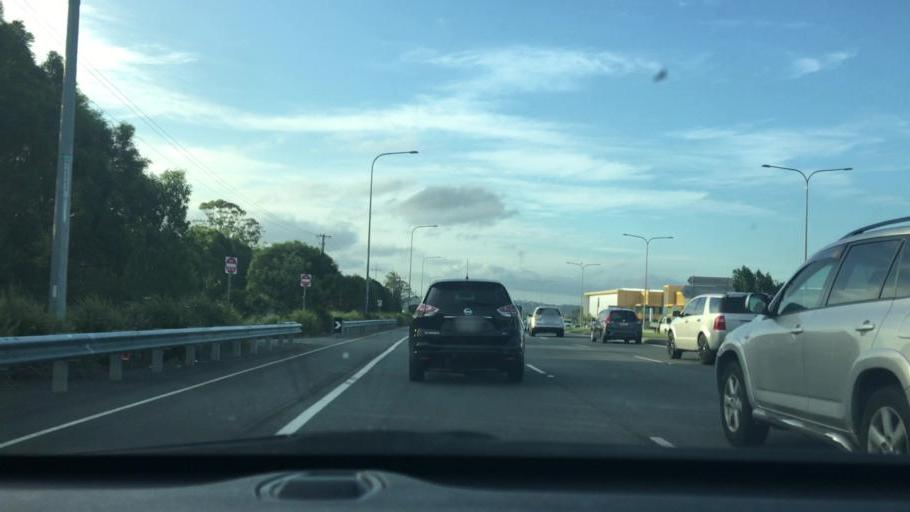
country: AU
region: Queensland
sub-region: Gold Coast
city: Nerang
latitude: -28.0084
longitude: 153.3659
